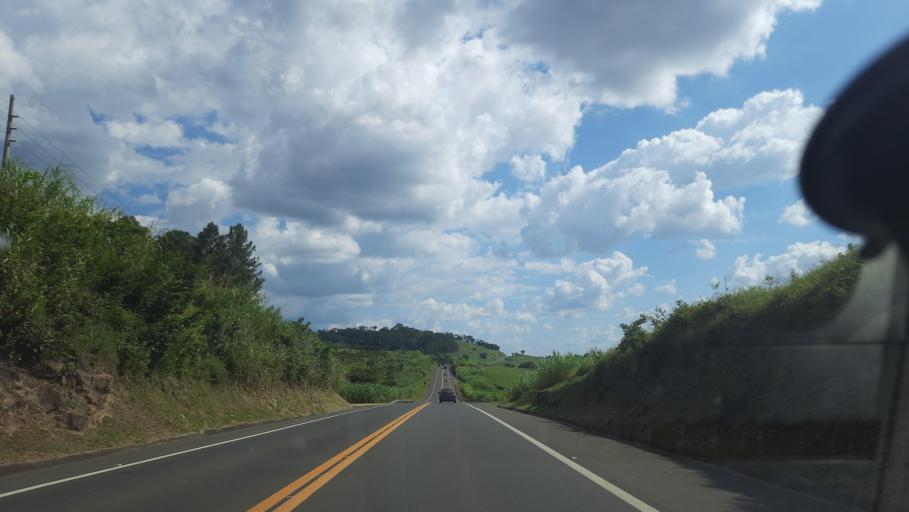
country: BR
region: Sao Paulo
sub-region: Sao Jose Do Rio Pardo
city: Sao Jose do Rio Pardo
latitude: -21.6423
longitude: -46.9068
